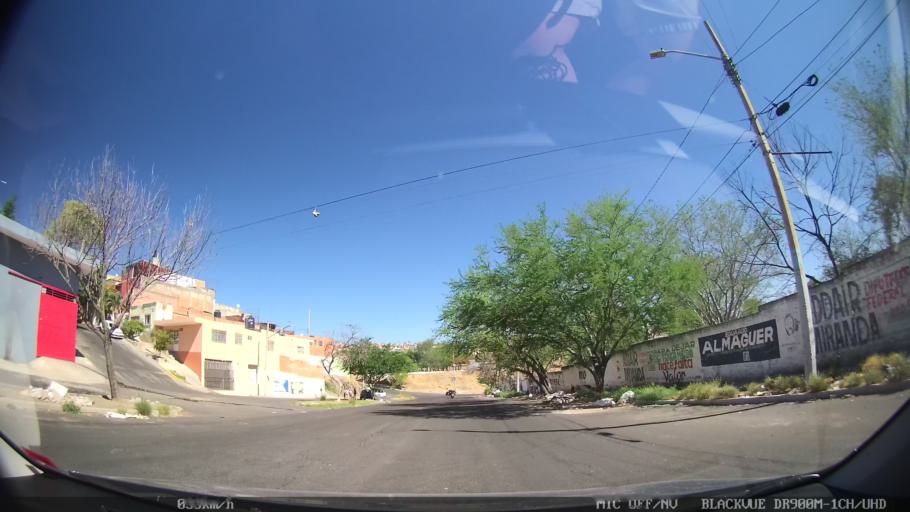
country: MX
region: Jalisco
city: Tlaquepaque
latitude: 20.7025
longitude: -103.2859
